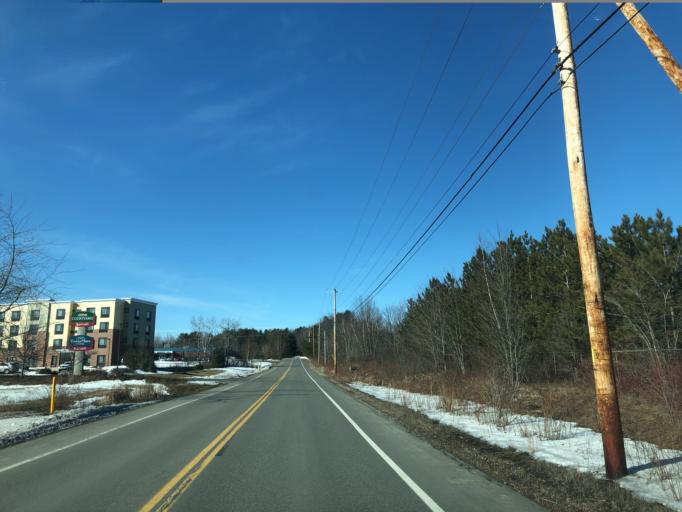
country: US
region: Maine
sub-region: Penobscot County
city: Brewer
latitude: 44.8263
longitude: -68.7498
